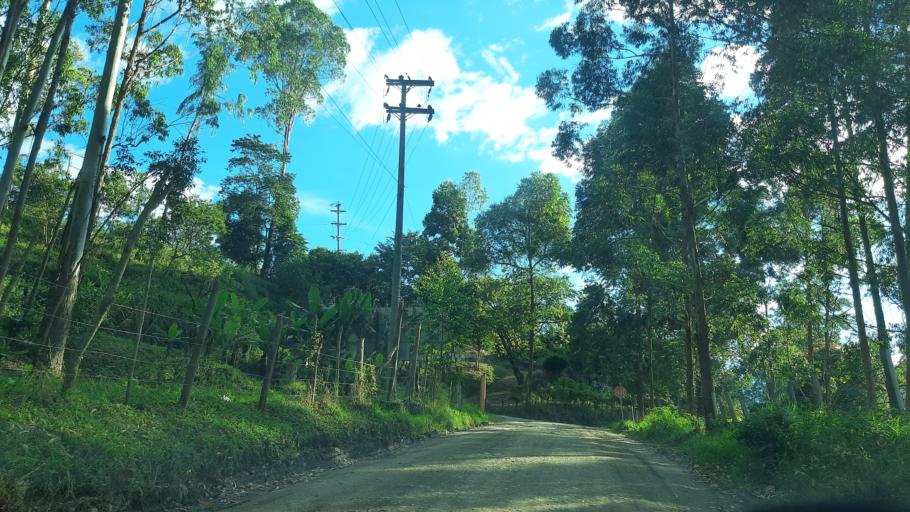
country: CO
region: Boyaca
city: Garagoa
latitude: 5.0778
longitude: -73.3735
